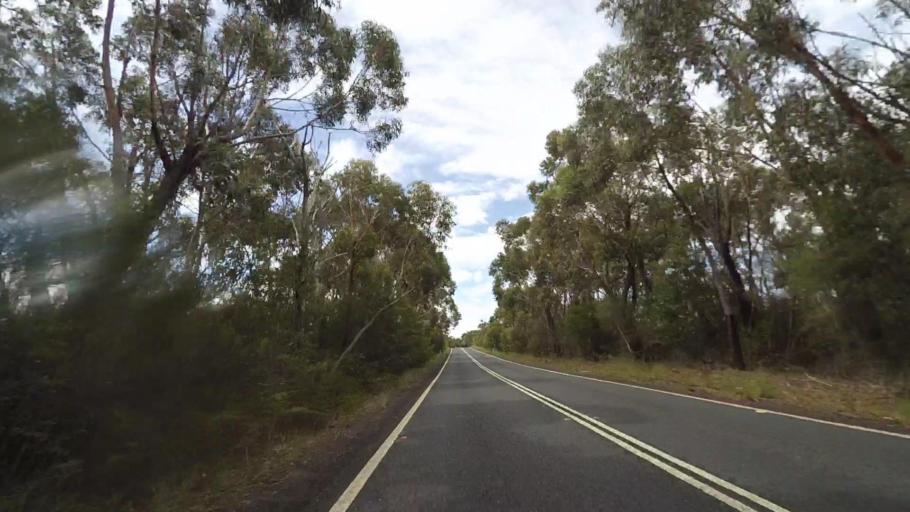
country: AU
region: New South Wales
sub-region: Sutherland Shire
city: Grays Point
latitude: -34.0919
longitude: 151.0636
